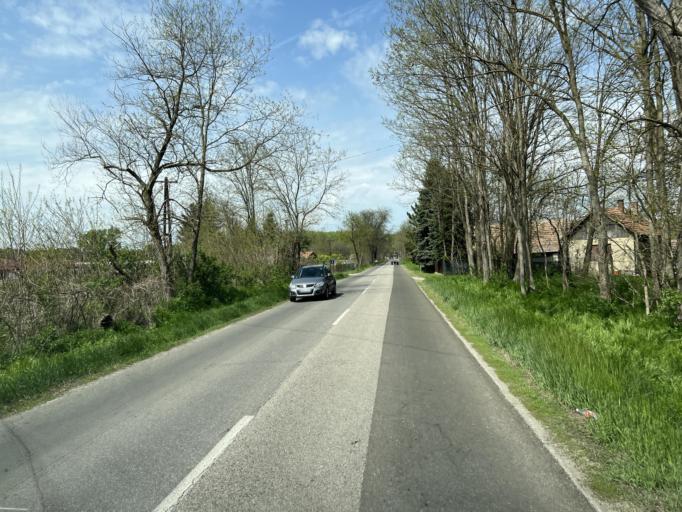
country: HU
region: Pest
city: Albertirsa
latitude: 47.2164
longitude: 19.6095
